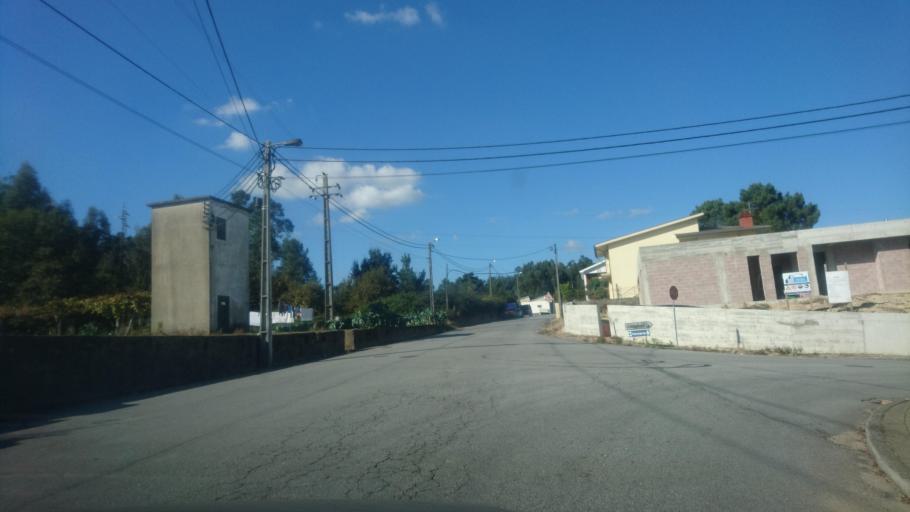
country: PT
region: Porto
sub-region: Paredes
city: Madalena
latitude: 41.2204
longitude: -8.3383
